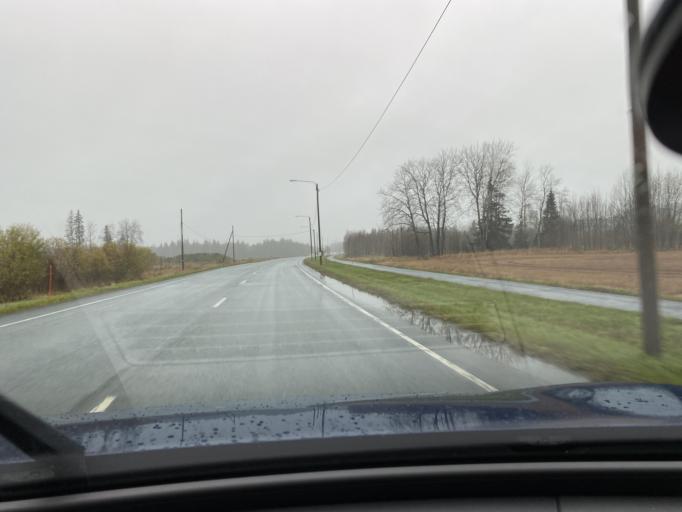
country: FI
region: Haeme
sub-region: Forssa
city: Forssa
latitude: 60.8010
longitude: 23.5668
